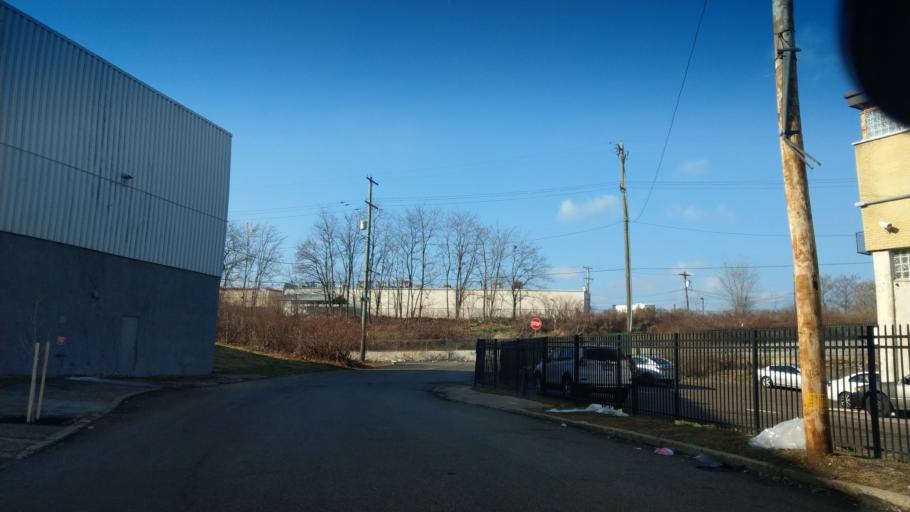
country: US
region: Pennsylvania
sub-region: Philadelphia County
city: Philadelphia
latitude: 40.0151
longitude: -75.1289
